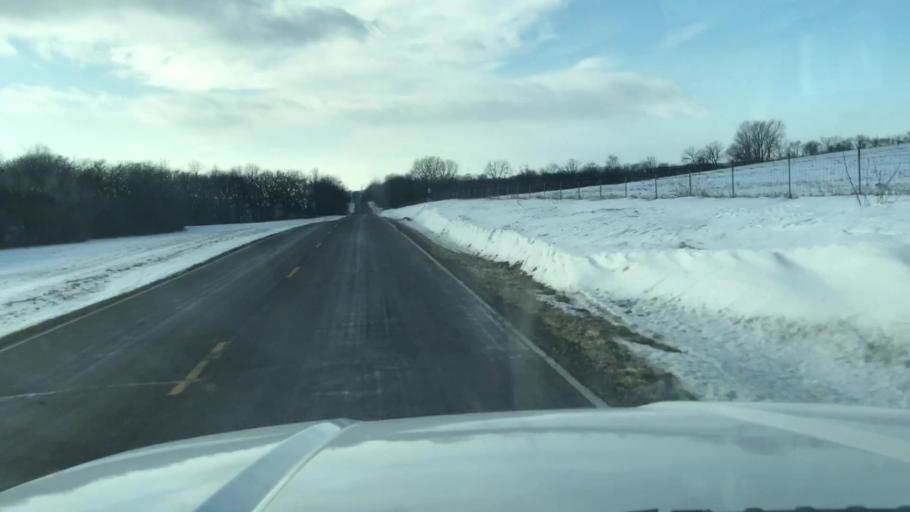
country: US
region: Missouri
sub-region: Nodaway County
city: Maryville
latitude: 40.2019
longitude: -94.9395
